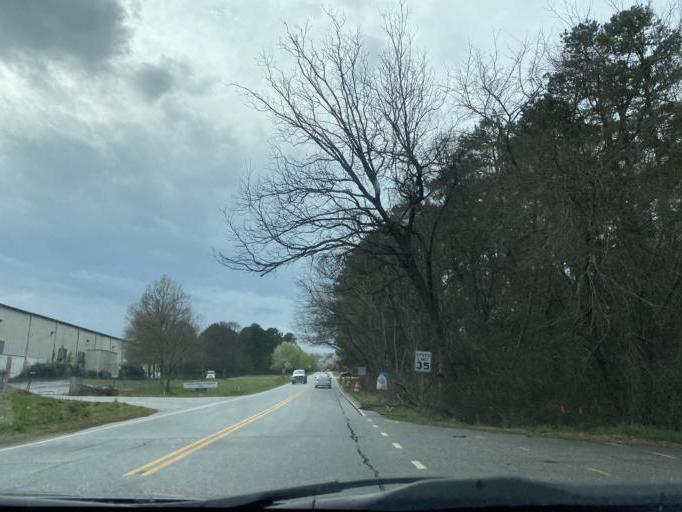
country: US
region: South Carolina
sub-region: Spartanburg County
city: Cowpens
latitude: 35.0222
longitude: -81.7896
